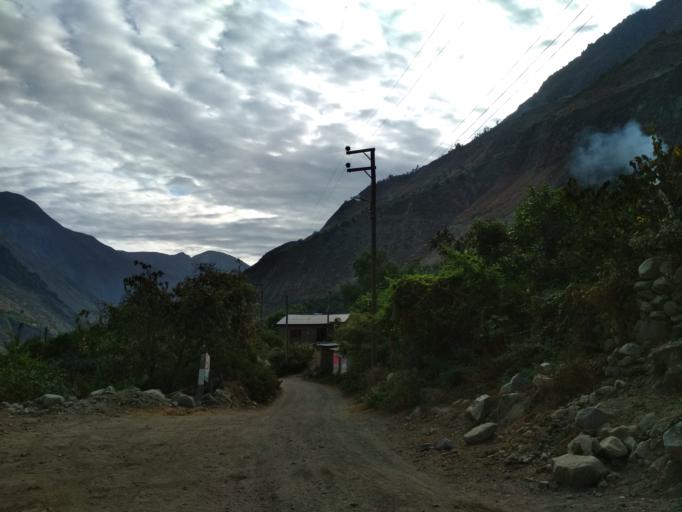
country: PE
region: Lima
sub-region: Provincia de Yauyos
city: Cacra
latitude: -12.8230
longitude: -75.7935
